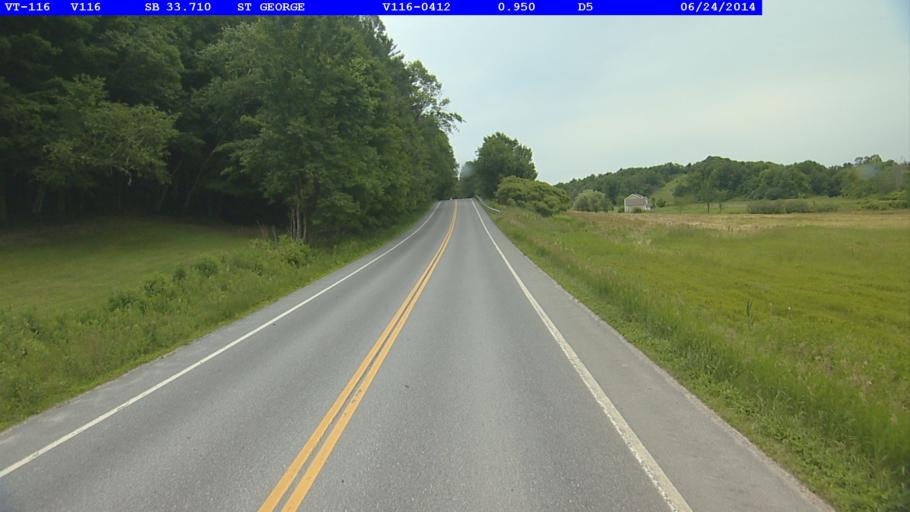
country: US
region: Vermont
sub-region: Chittenden County
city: Hinesburg
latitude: 44.3768
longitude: -73.1356
